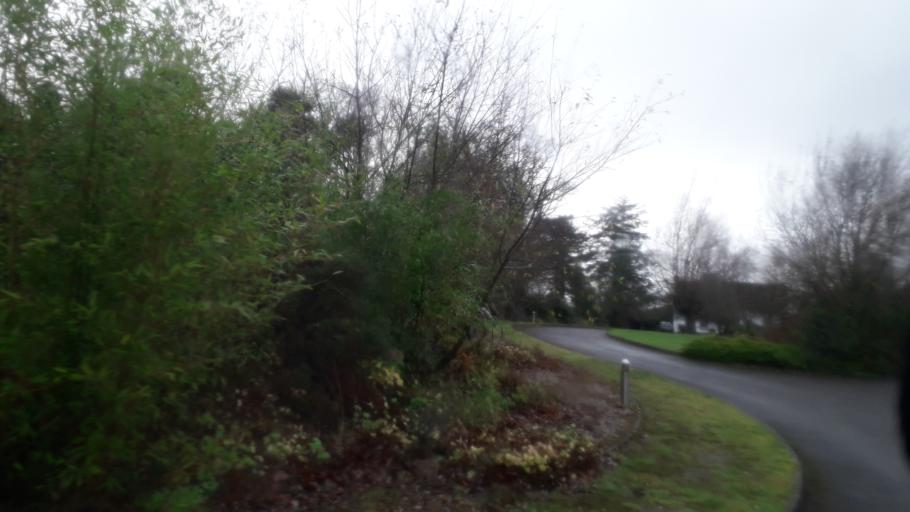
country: IE
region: Ulster
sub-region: County Donegal
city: Buncrana
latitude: 55.0989
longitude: -7.5365
